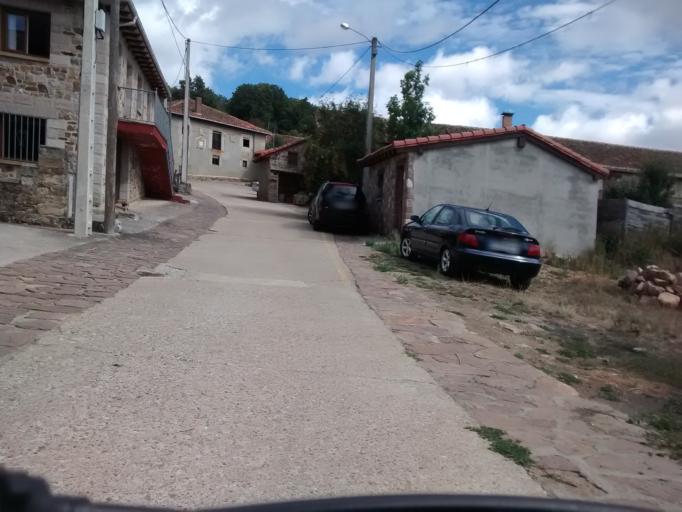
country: ES
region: Castille and Leon
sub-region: Provincia de Palencia
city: Polentinos
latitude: 42.9421
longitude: -4.4614
